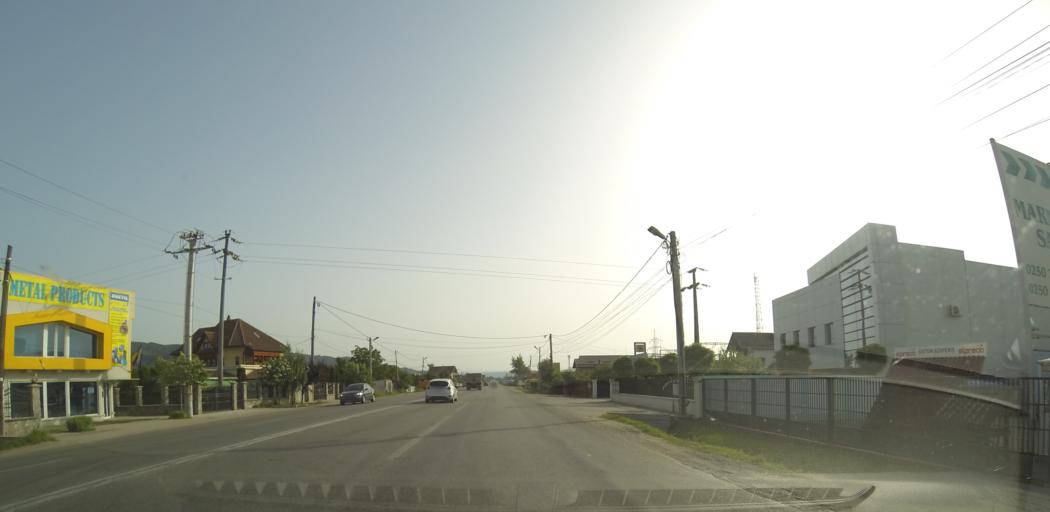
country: RO
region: Valcea
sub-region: Municipiul Ramnicu Valcea
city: Copacelu
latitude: 45.0630
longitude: 24.3373
